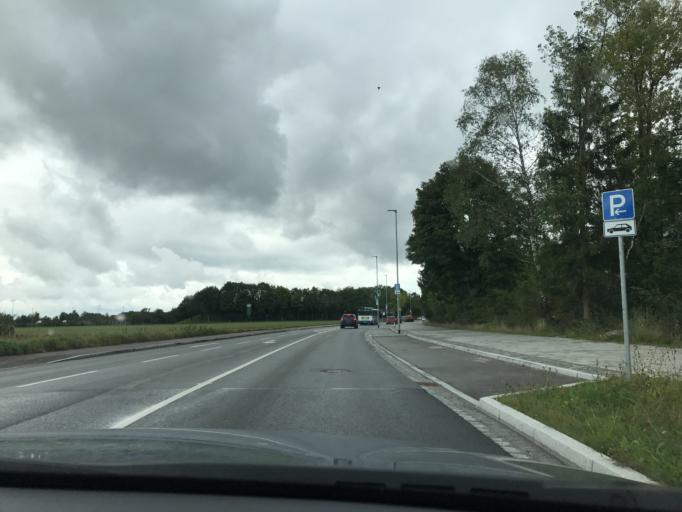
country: DE
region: Bavaria
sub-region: Upper Bavaria
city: Ottobrunn
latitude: 48.0537
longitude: 11.6505
